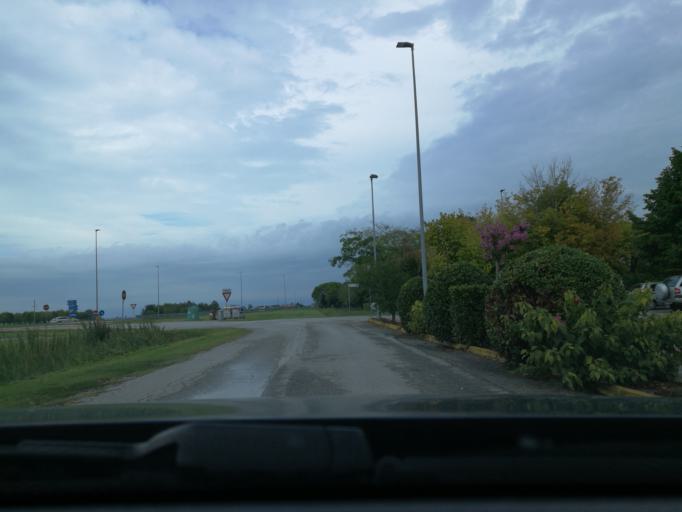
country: IT
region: Friuli Venezia Giulia
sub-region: Provincia di Udine
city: Pertegada
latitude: 45.7225
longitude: 13.0686
